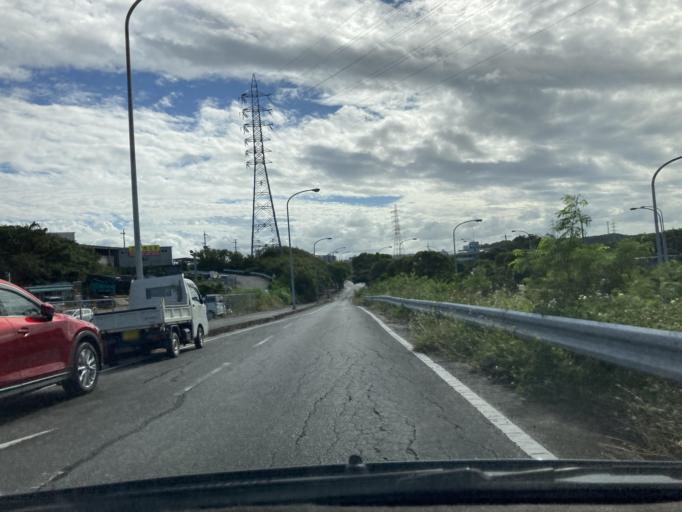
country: JP
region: Okinawa
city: Tomigusuku
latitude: 26.1729
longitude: 127.7273
